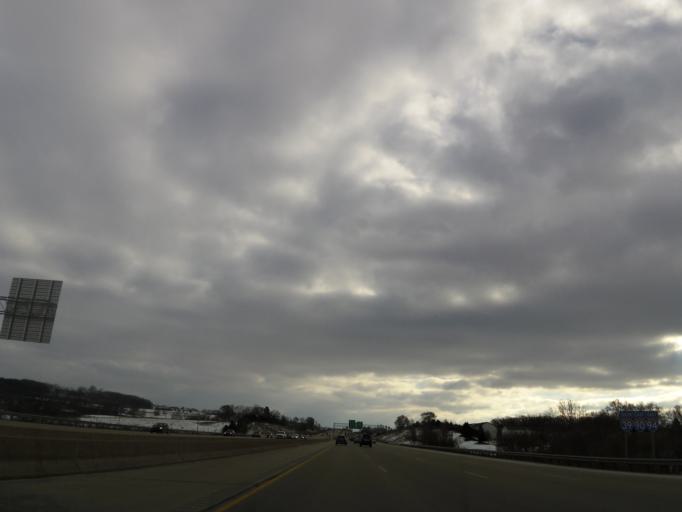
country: US
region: Wisconsin
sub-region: Dane County
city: Monona
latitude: 43.1235
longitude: -89.2901
